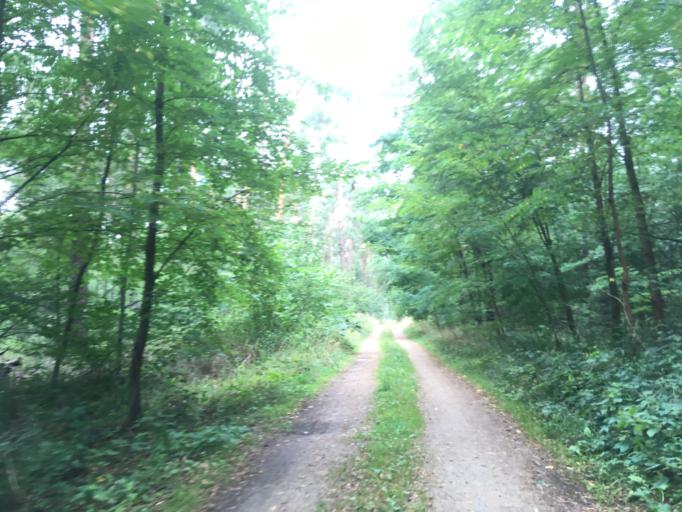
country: DE
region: Brandenburg
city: Wildau
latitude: 52.3260
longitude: 13.7034
